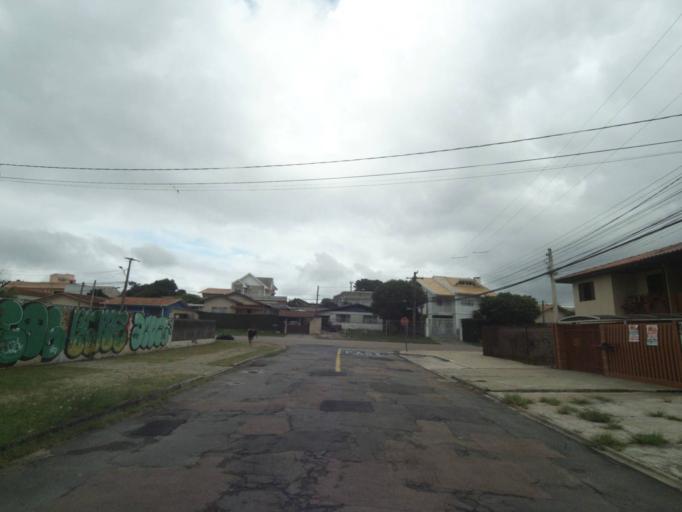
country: BR
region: Parana
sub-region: Curitiba
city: Curitiba
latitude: -25.4908
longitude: -49.2856
